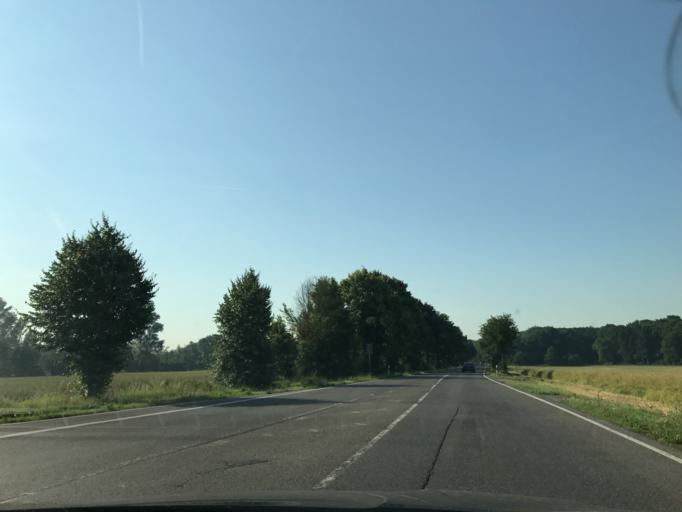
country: DE
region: North Rhine-Westphalia
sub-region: Regierungsbezirk Dusseldorf
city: Meerbusch
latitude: 51.2783
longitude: 6.6618
